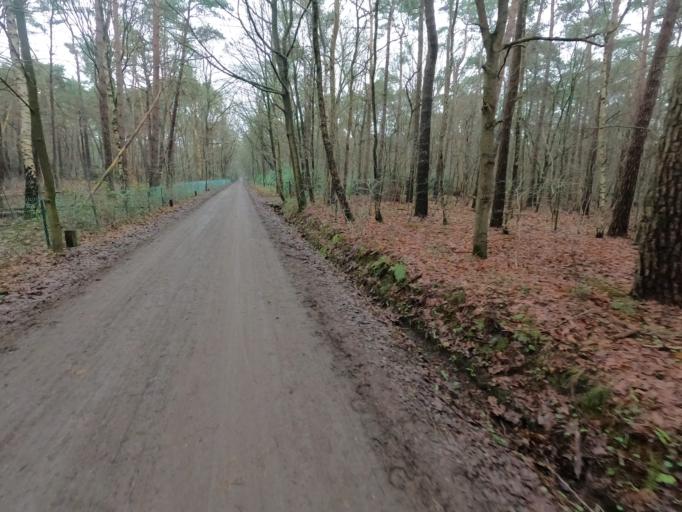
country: BE
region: Flanders
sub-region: Provincie Antwerpen
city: Schilde
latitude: 51.2956
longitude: 4.5944
